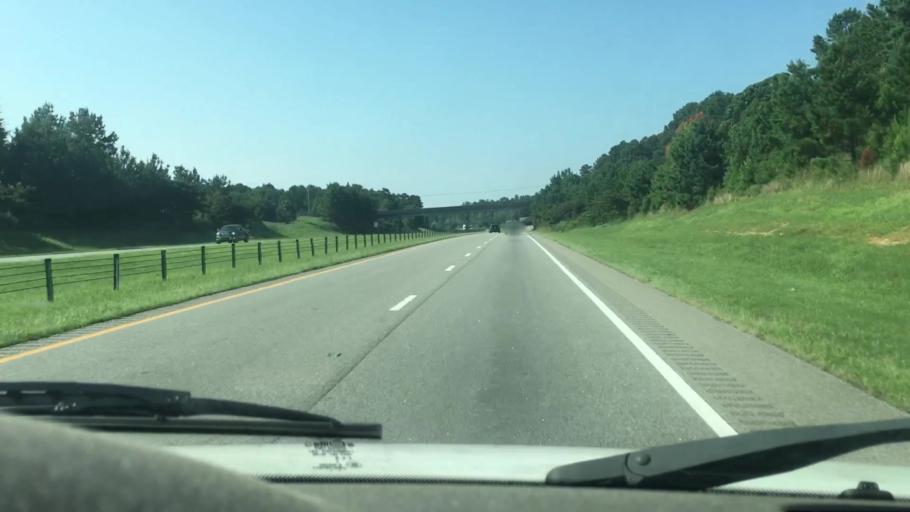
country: US
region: North Carolina
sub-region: Lincoln County
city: Lowesville
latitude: 35.3908
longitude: -80.9991
